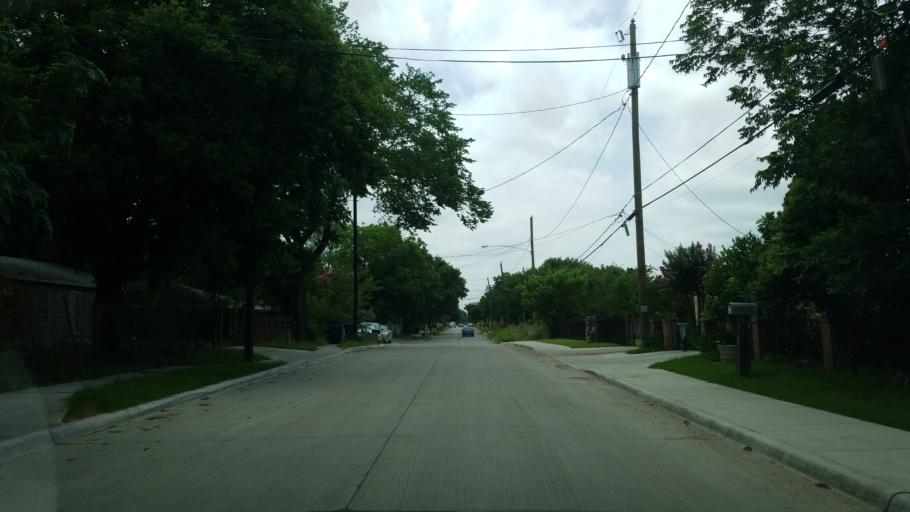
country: US
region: Texas
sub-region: Dallas County
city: Irving
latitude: 32.7923
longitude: -96.9025
